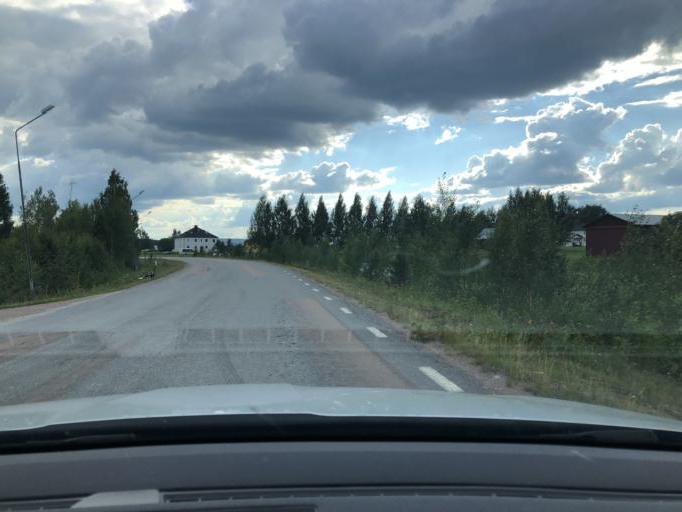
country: SE
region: Vaesternorrland
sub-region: Solleftea Kommun
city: Solleftea
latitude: 63.1888
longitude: 17.0700
